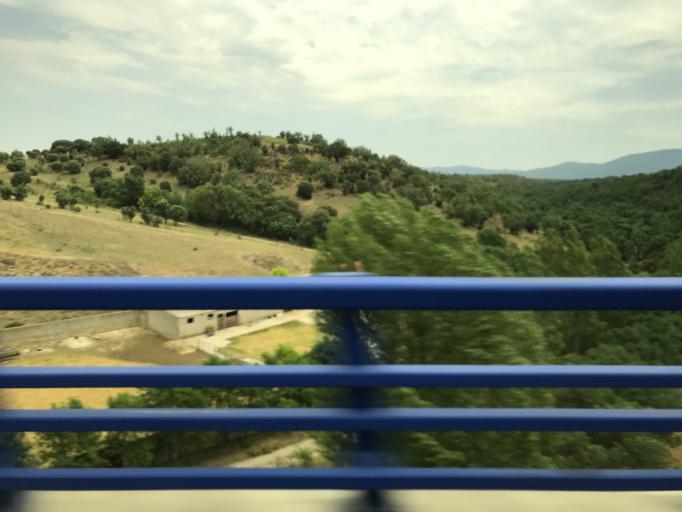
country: ES
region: Castille and Leon
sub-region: Provincia de Segovia
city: Cerezo de Abajo
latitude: 41.2164
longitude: -3.5815
